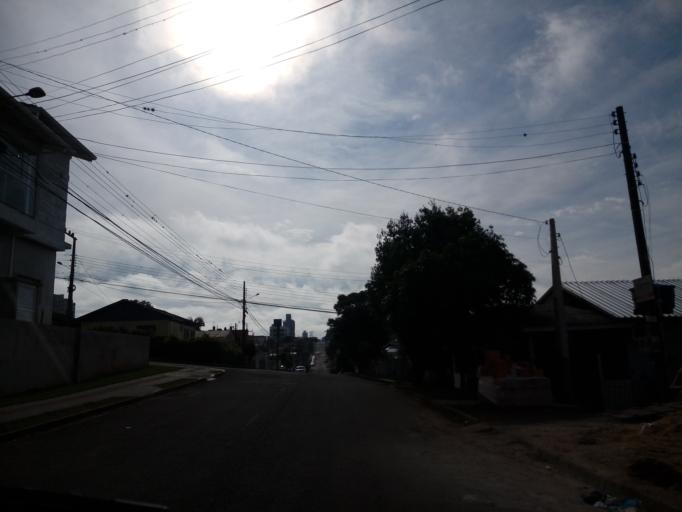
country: BR
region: Santa Catarina
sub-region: Chapeco
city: Chapeco
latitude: -27.1009
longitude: -52.6388
